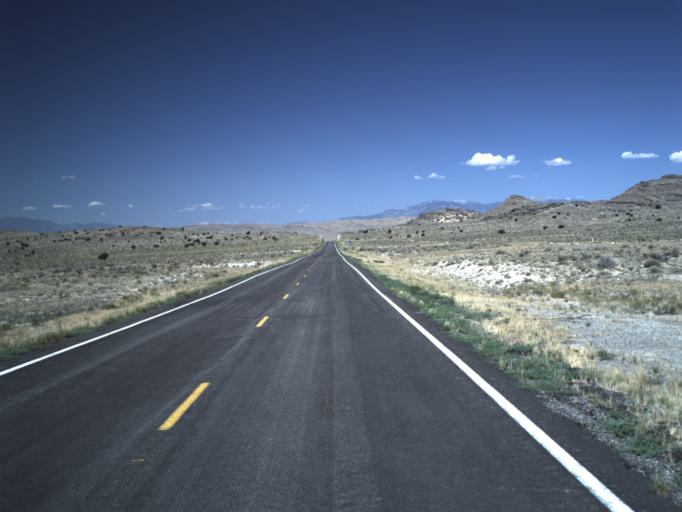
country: US
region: Utah
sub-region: Beaver County
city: Milford
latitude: 39.0769
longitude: -113.6868
